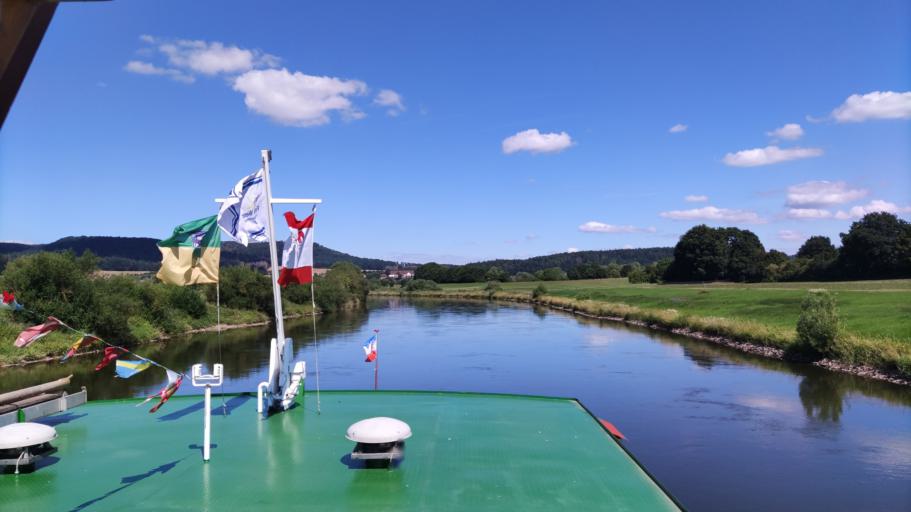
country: DE
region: North Rhine-Westphalia
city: Beverungen
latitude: 51.6796
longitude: 9.3963
